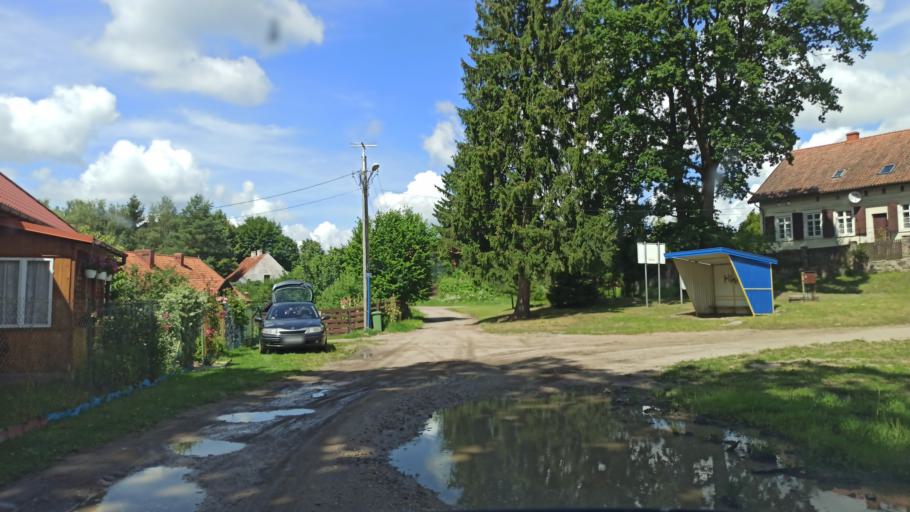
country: PL
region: Warmian-Masurian Voivodeship
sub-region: Powiat ostrodzki
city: Milakowo
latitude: 53.8592
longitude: 20.0654
